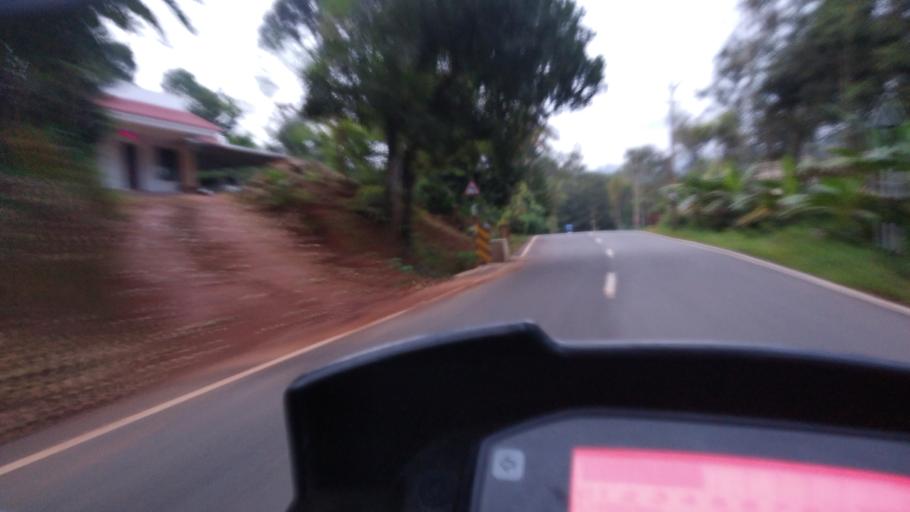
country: IN
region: Kerala
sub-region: Idukki
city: Munnar
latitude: 9.9679
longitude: 77.1341
